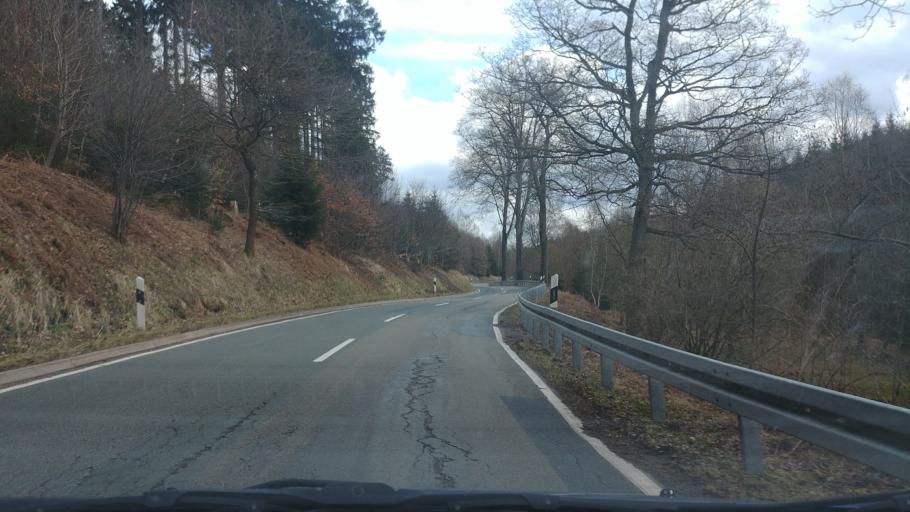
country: DE
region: Lower Saxony
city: Derental
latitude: 51.7554
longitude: 9.4555
